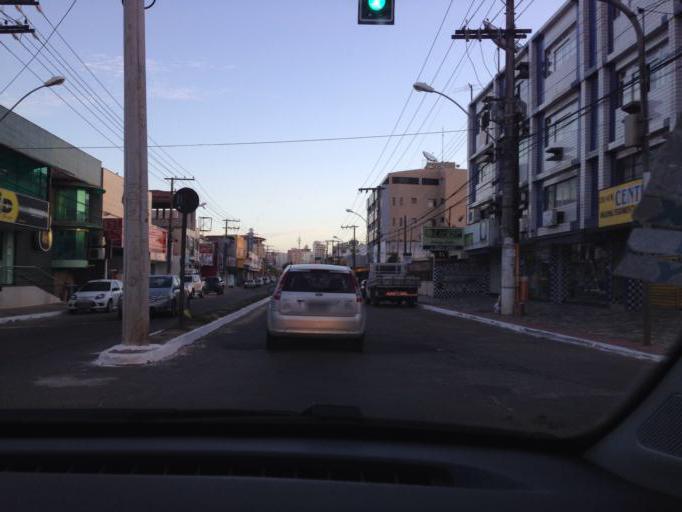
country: BR
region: Espirito Santo
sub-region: Guarapari
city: Guarapari
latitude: -20.6624
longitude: -40.5013
